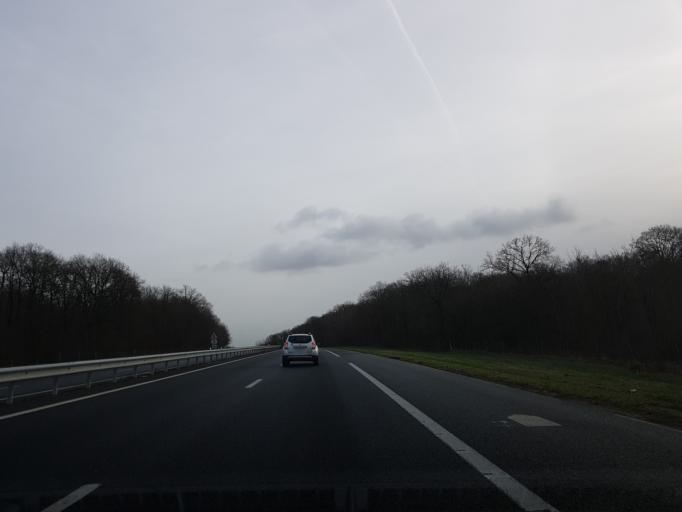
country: FR
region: Bourgogne
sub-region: Departement de l'Yonne
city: Soucy
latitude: 48.2366
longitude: 3.3771
